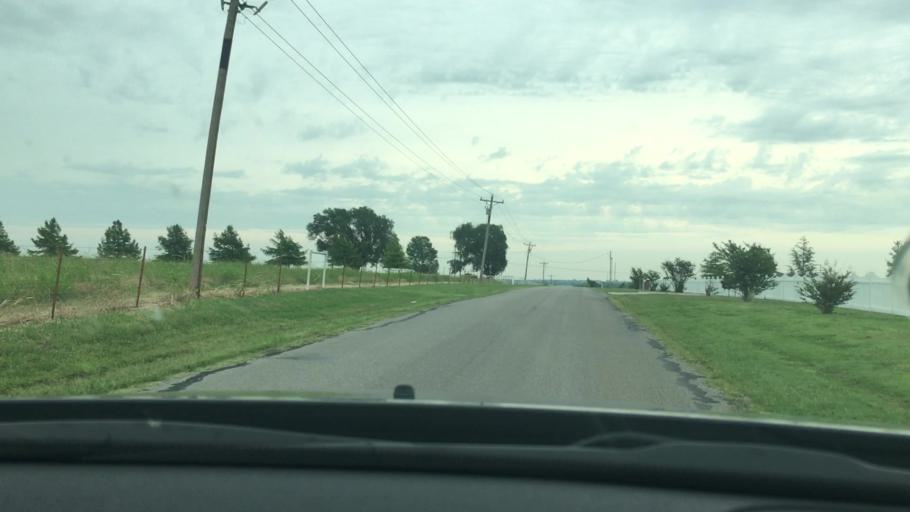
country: US
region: Oklahoma
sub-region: Murray County
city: Sulphur
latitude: 34.5353
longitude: -96.9794
